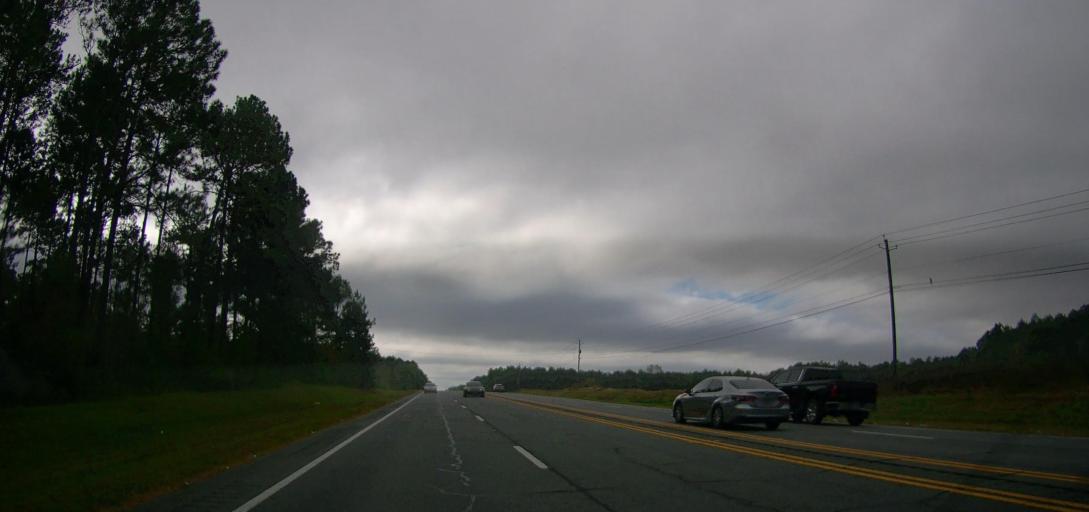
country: US
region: Georgia
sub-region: Colquitt County
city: Moultrie
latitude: 31.2392
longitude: -83.7329
